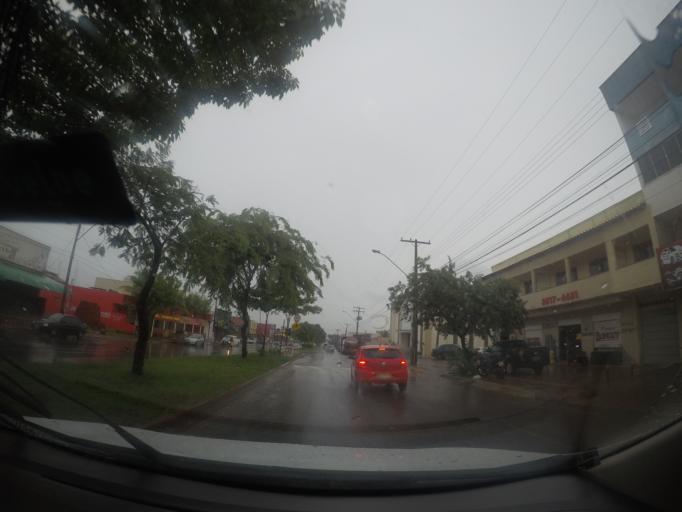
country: BR
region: Goias
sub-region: Goiania
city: Goiania
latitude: -16.6270
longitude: -49.3323
